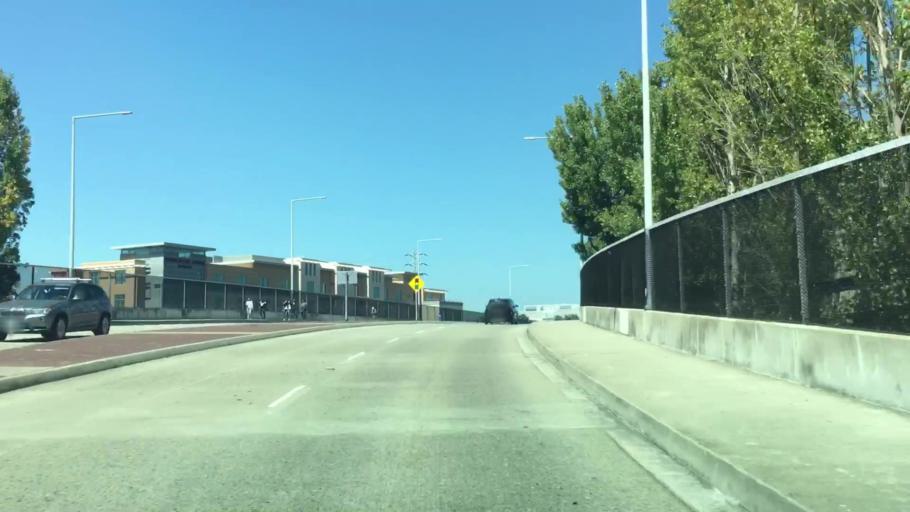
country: US
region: California
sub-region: San Mateo County
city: Foster City
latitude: 37.5599
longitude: -122.2779
